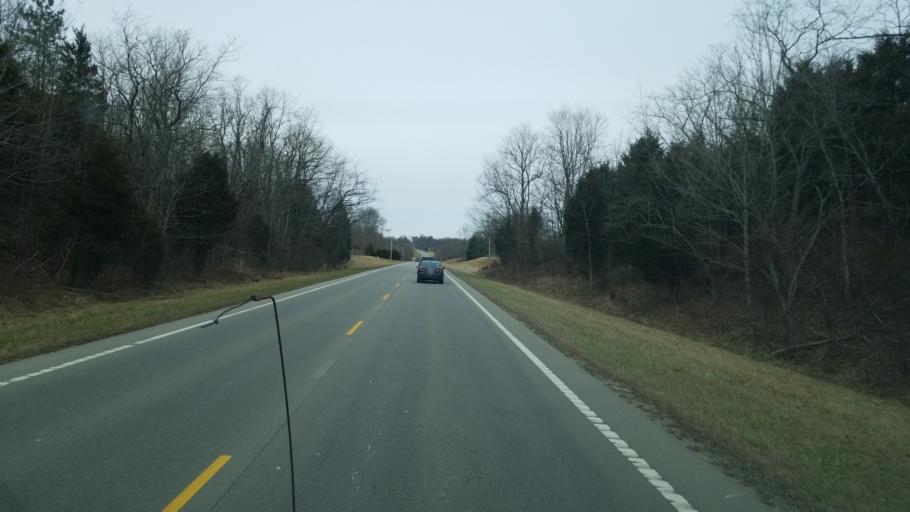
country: US
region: Ohio
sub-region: Highland County
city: Hillsboro
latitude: 39.1204
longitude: -83.6736
